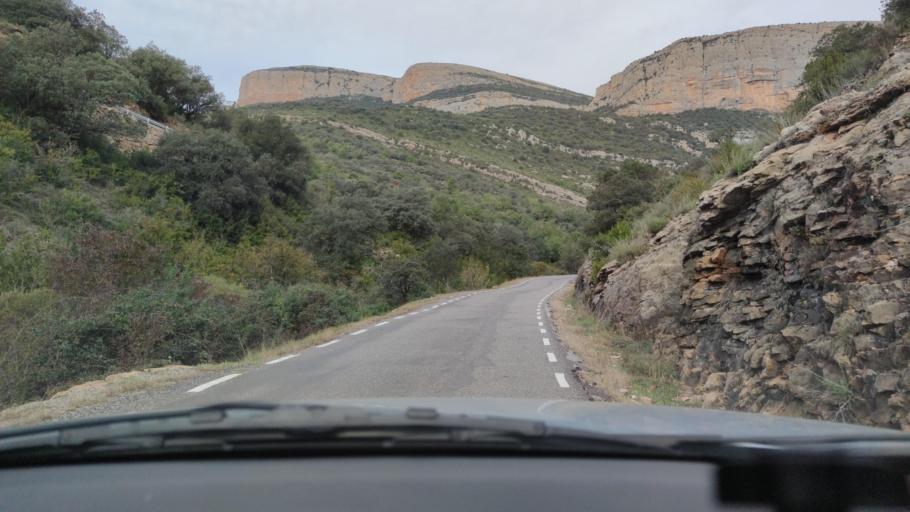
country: ES
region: Catalonia
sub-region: Provincia de Lleida
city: Artesa de Segre
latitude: 42.0125
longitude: 1.0317
